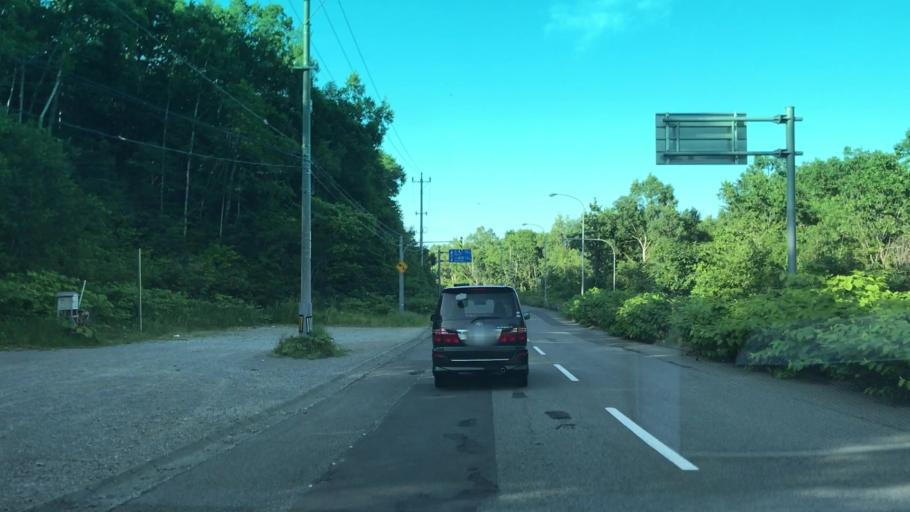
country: JP
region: Hokkaido
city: Otaru
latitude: 43.1339
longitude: 141.0122
